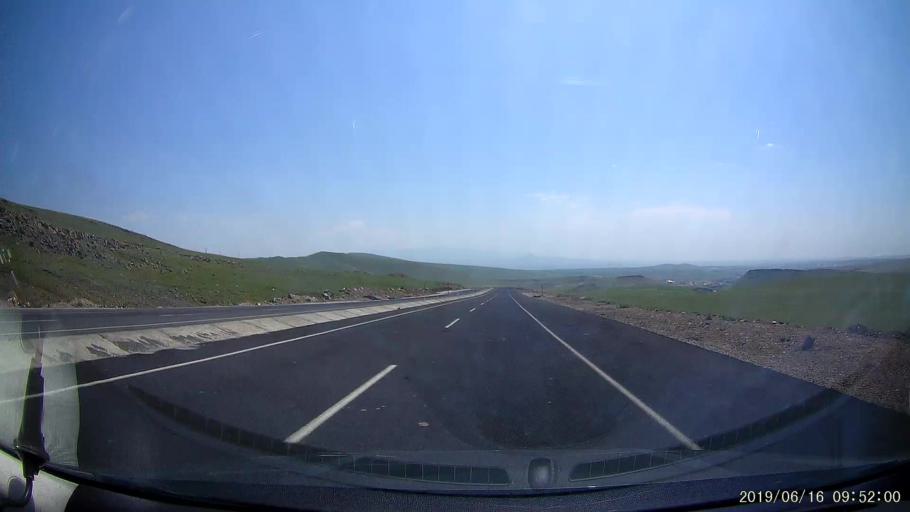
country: TR
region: Kars
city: Digor
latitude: 40.3924
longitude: 43.3772
